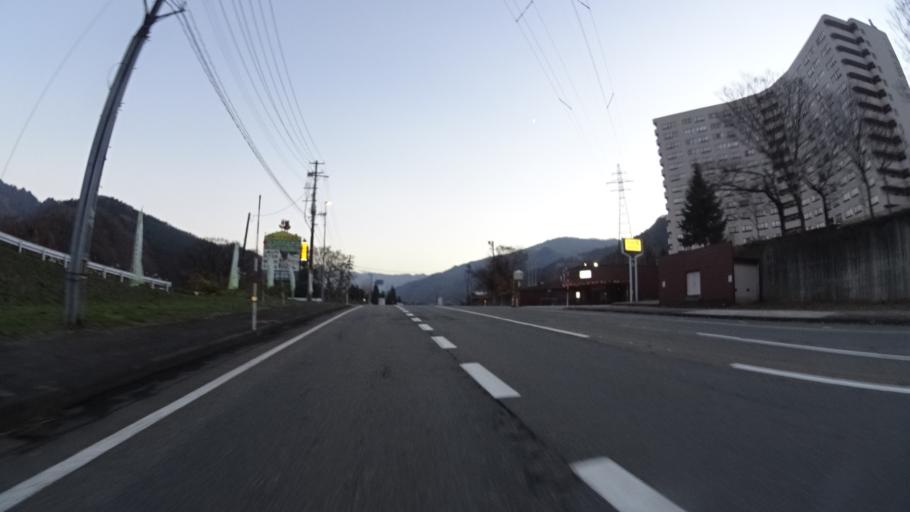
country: JP
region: Niigata
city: Shiozawa
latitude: 36.9677
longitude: 138.8016
